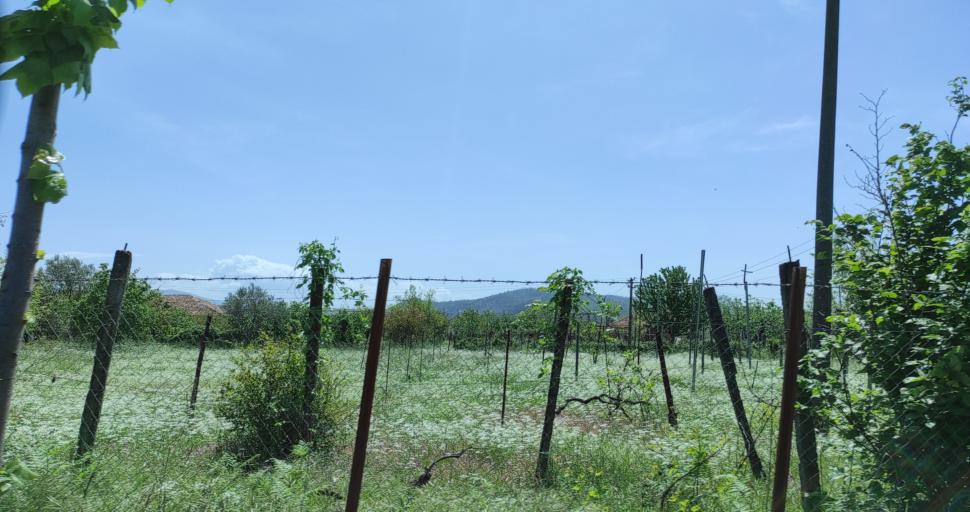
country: AL
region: Shkoder
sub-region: Rrethi i Shkodres
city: Shkoder
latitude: 42.1051
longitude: 19.5580
